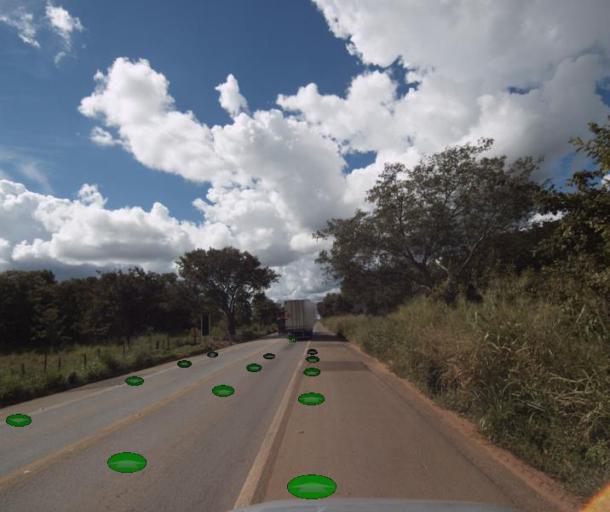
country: BR
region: Goias
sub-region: Porangatu
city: Porangatu
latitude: -13.4398
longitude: -49.1325
